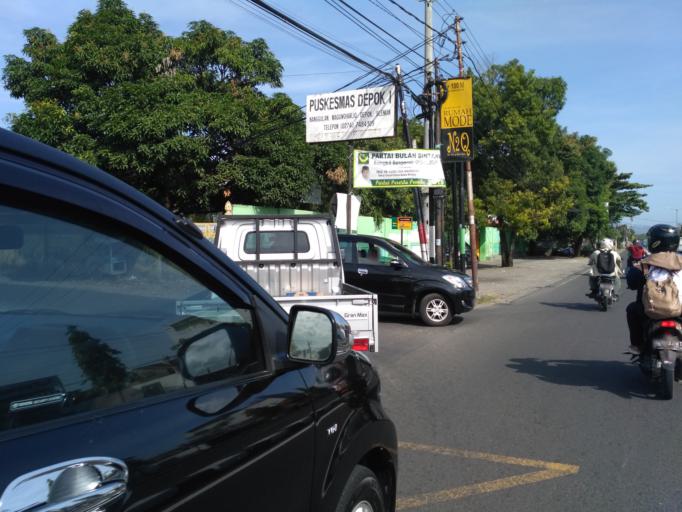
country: ID
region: Daerah Istimewa Yogyakarta
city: Depok
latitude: -7.7746
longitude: 110.4307
